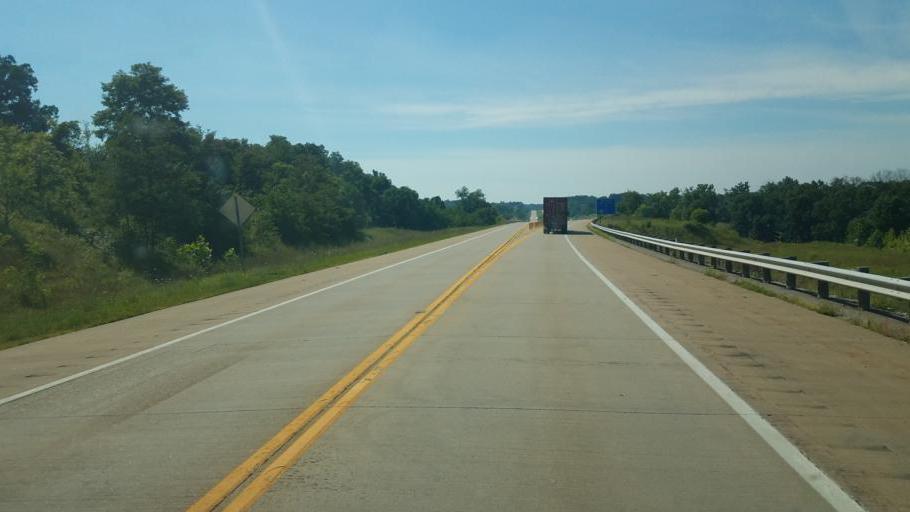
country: US
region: West Virginia
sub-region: Mason County
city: New Haven
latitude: 39.0474
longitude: -81.9624
